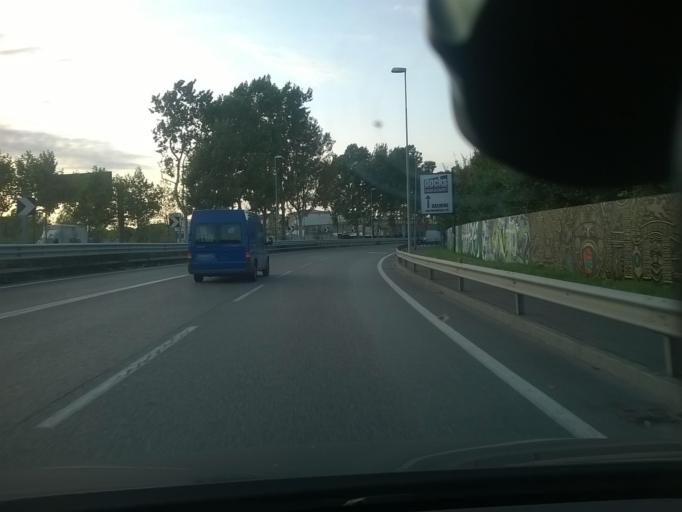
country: IT
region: Lombardy
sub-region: Provincia di Bergamo
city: Gorle
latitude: 45.7015
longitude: 9.6957
